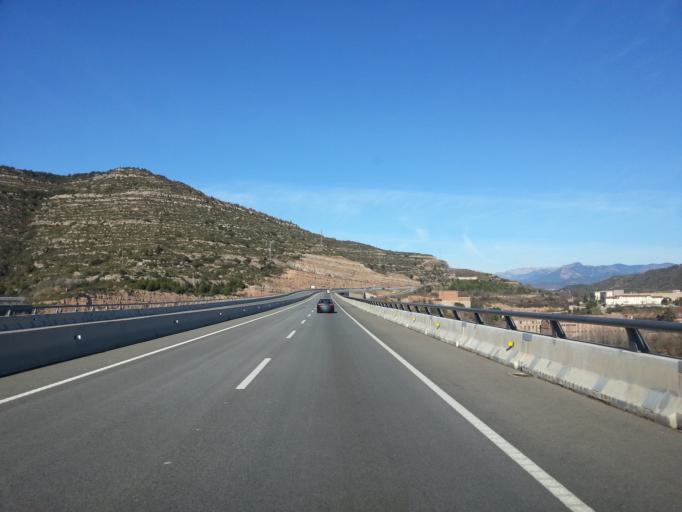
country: ES
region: Catalonia
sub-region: Provincia de Barcelona
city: Puig-reig
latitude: 41.9825
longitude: 1.8855
